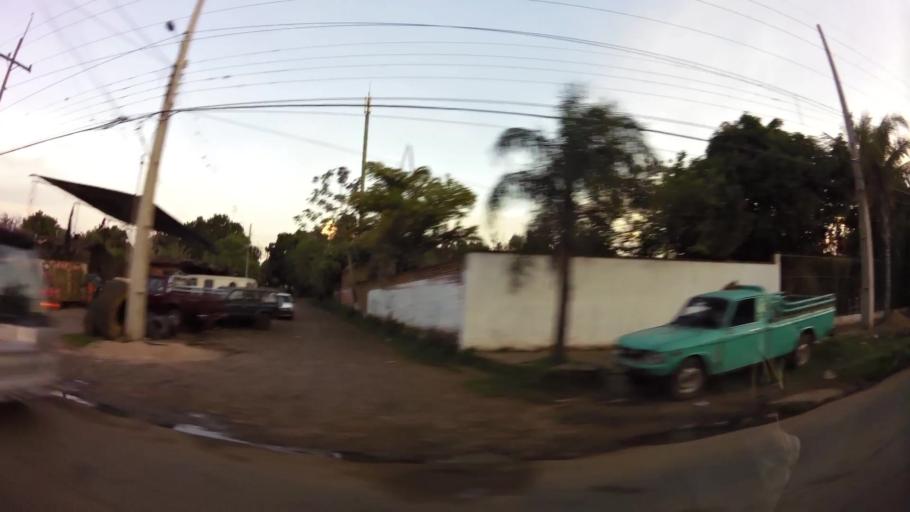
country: PY
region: Central
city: Nemby
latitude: -25.3896
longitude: -57.5010
